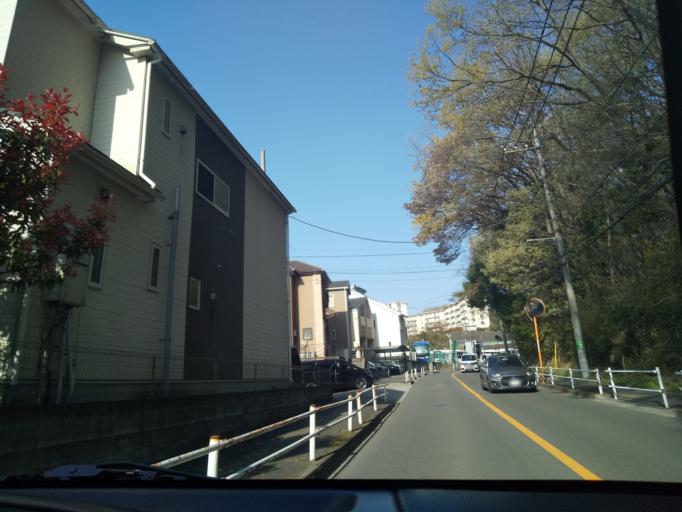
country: JP
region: Tokyo
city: Hino
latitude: 35.6455
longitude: 139.4209
